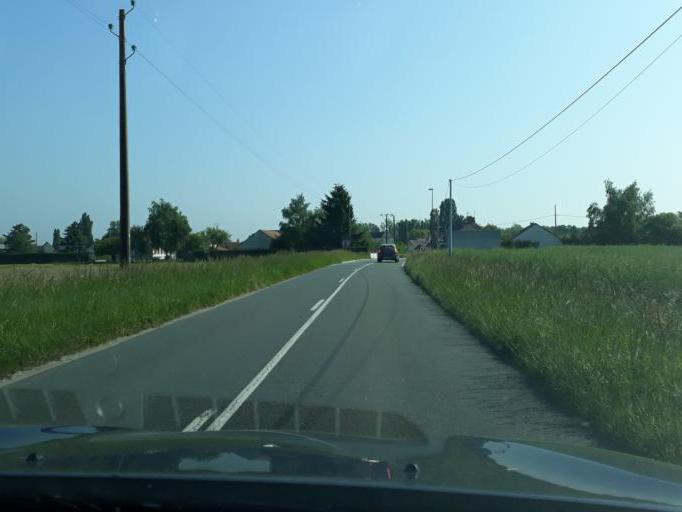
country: FR
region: Centre
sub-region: Departement du Loiret
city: Trainou
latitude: 47.9619
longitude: 2.0943
